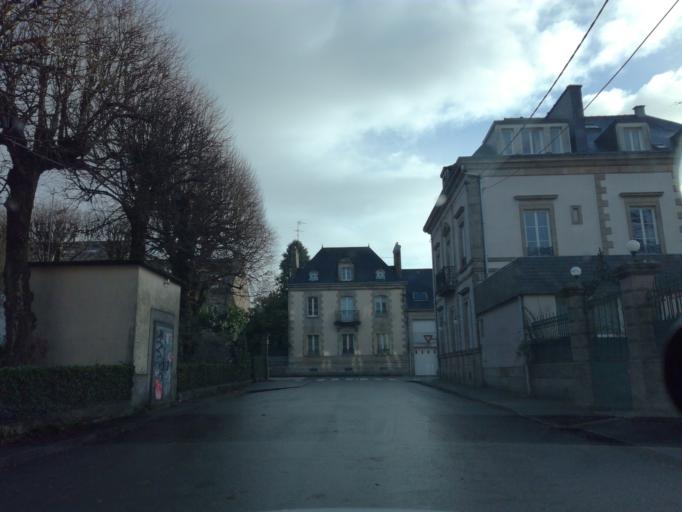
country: FR
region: Brittany
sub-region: Departement du Morbihan
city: Pontivy
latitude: 48.0626
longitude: -2.9676
